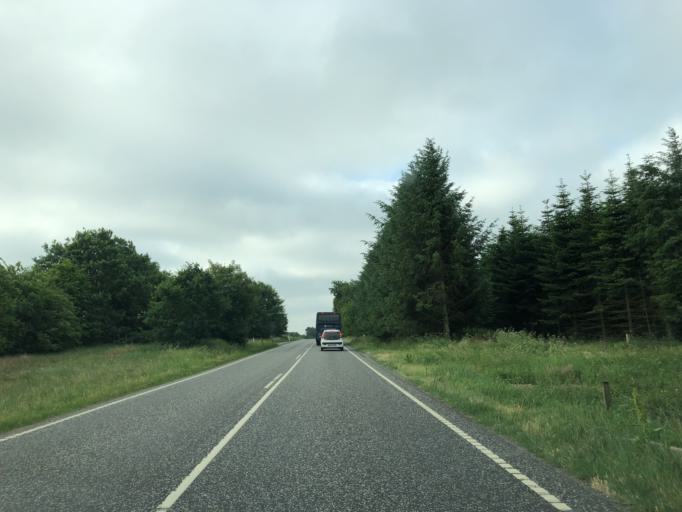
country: DK
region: South Denmark
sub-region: Vejle Kommune
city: Give
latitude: 55.7814
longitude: 9.2778
